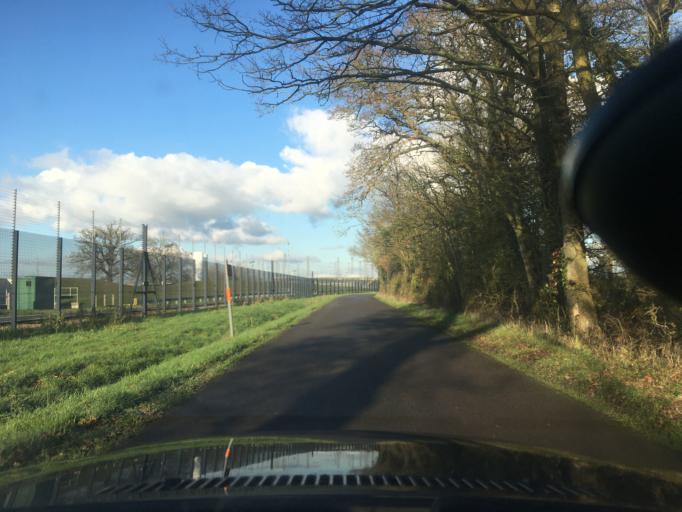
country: GB
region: England
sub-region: West Berkshire
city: Stratfield Mortimer
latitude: 51.4035
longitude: -1.0207
